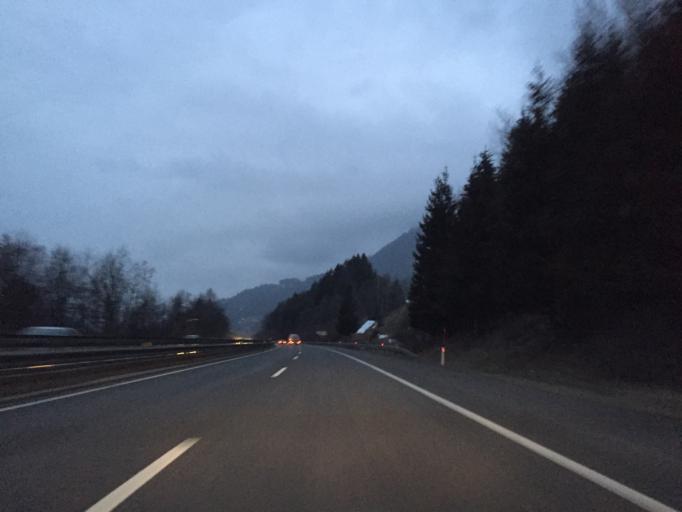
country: AT
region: Salzburg
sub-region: Politischer Bezirk Sankt Johann im Pongau
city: Eben im Pongau
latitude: 47.4239
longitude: 13.3647
